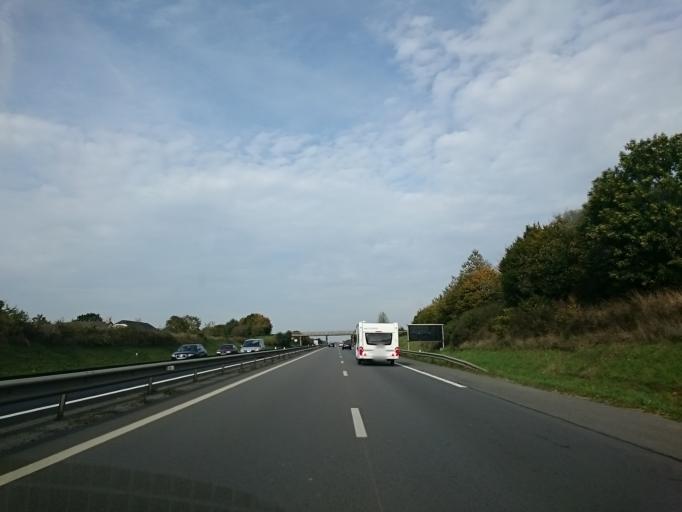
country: FR
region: Brittany
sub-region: Departement d'Ille-et-Vilaine
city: Chatillon-sur-Seiche
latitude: 48.0484
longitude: -1.6832
